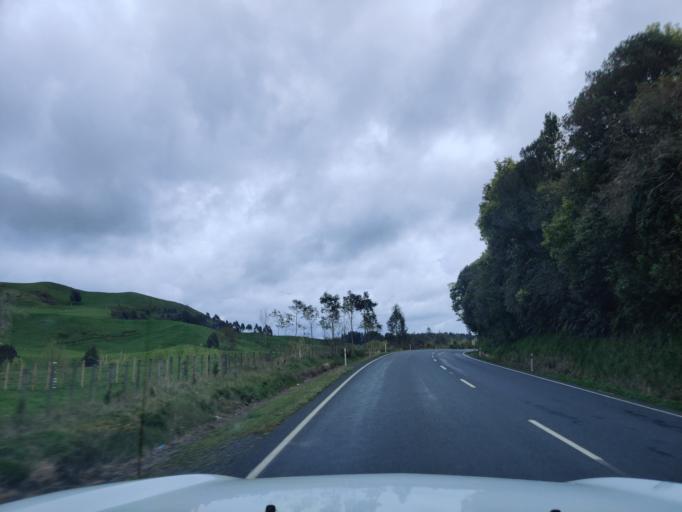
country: NZ
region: Waikato
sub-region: Otorohanga District
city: Otorohanga
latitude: -38.5357
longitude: 175.1778
